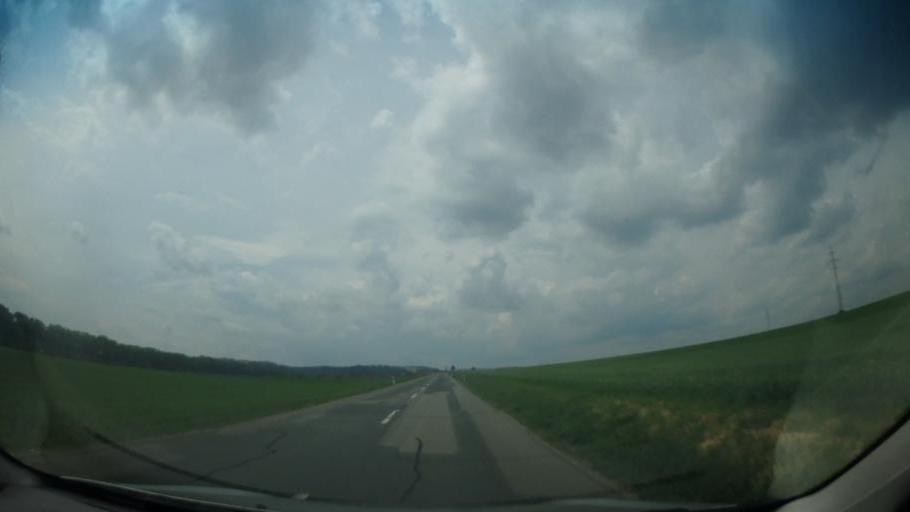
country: CZ
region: South Moravian
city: Boritov
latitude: 49.4322
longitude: 16.5738
